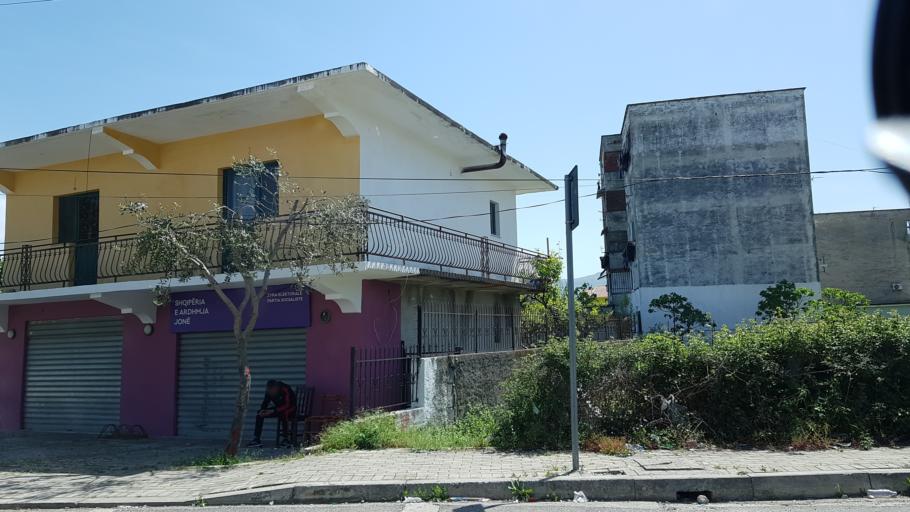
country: AL
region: Shkoder
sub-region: Rrethi i Malesia e Madhe
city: Kuc
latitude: 42.0534
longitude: 19.5225
